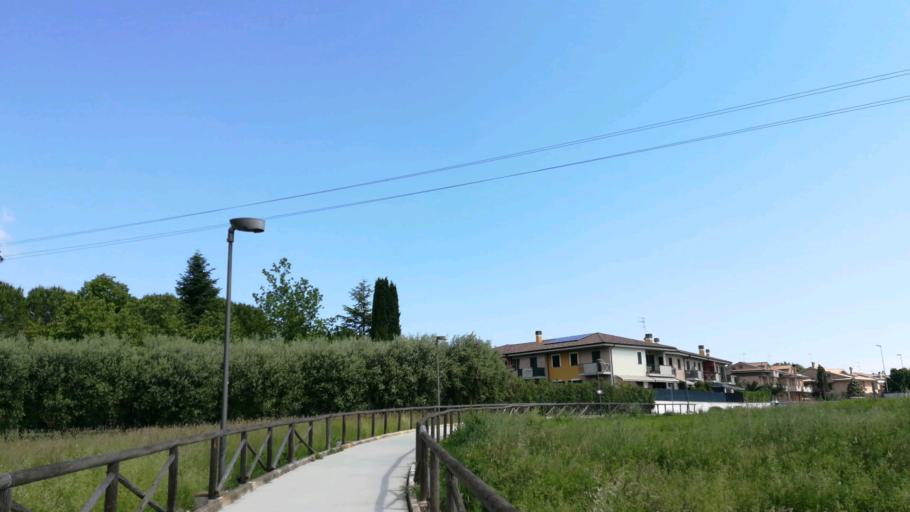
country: IT
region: The Marches
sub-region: Provincia di Macerata
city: Borgo Stazione
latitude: 43.2814
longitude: 13.6417
